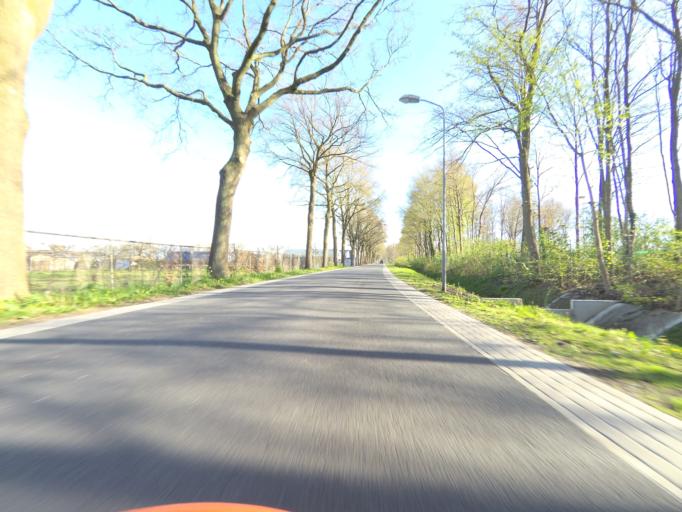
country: NL
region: Gelderland
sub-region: Gemeente Putten
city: Putten
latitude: 52.2487
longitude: 5.5903
